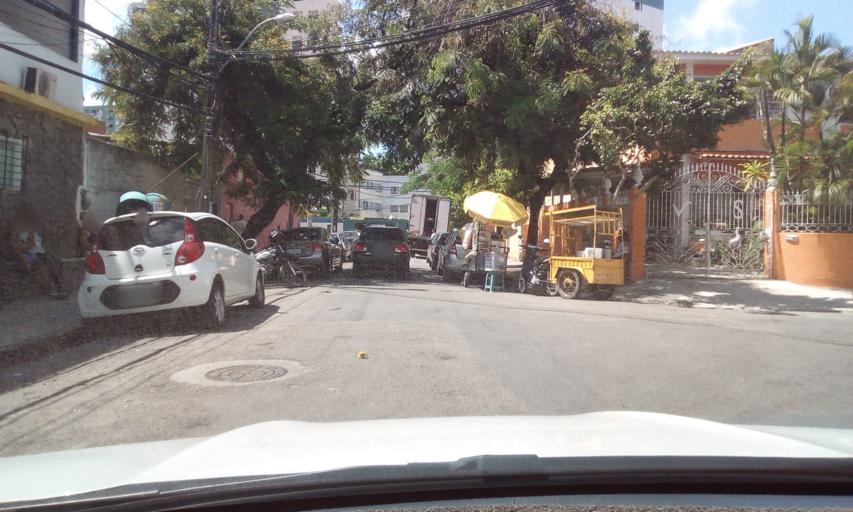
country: BR
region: Pernambuco
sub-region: Recife
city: Recife
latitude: -8.1333
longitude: -34.9047
